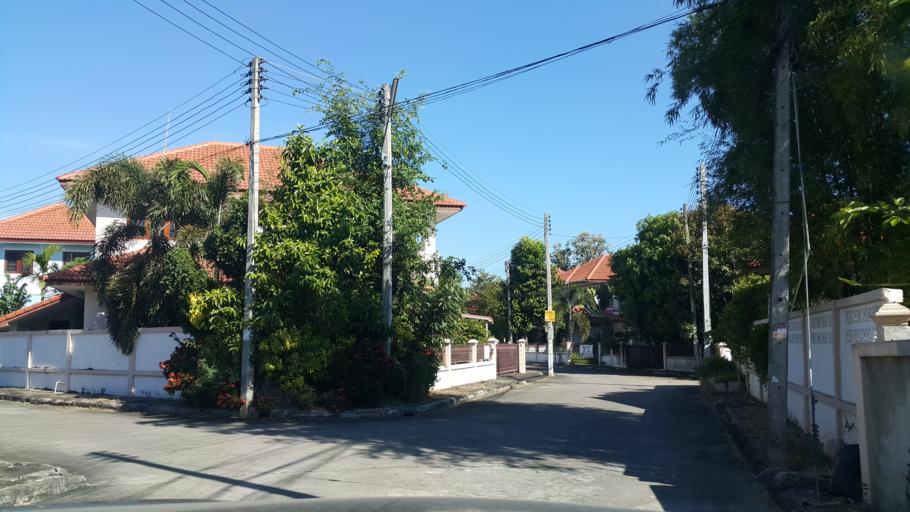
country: TH
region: Chiang Mai
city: San Sai
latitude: 18.8475
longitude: 98.9936
